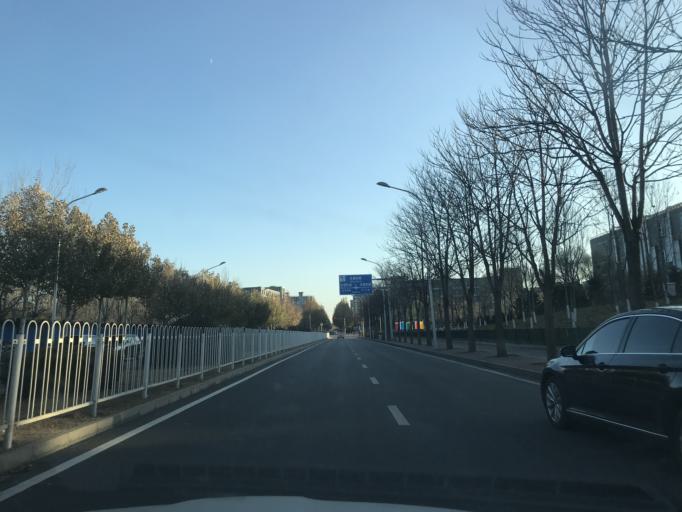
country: CN
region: Beijing
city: Xibeiwang
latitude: 40.0697
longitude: 116.2467
